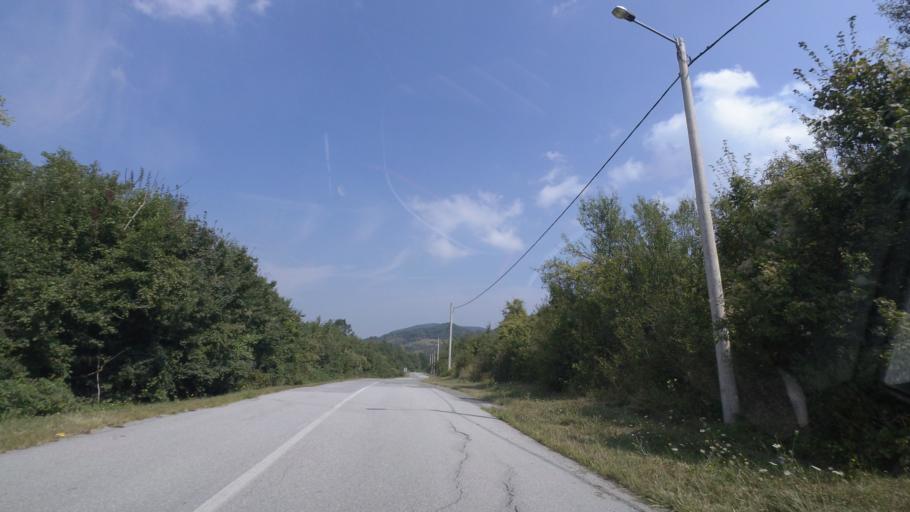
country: BA
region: Federation of Bosnia and Herzegovina
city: Zboriste
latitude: 45.1722
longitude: 16.1354
